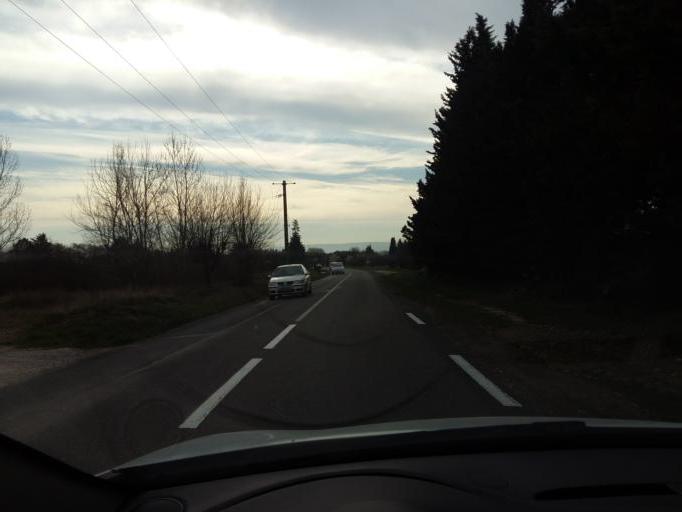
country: FR
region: Provence-Alpes-Cote d'Azur
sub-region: Departement du Vaucluse
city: L'Isle-sur-la-Sorgue
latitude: 43.9240
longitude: 5.0695
